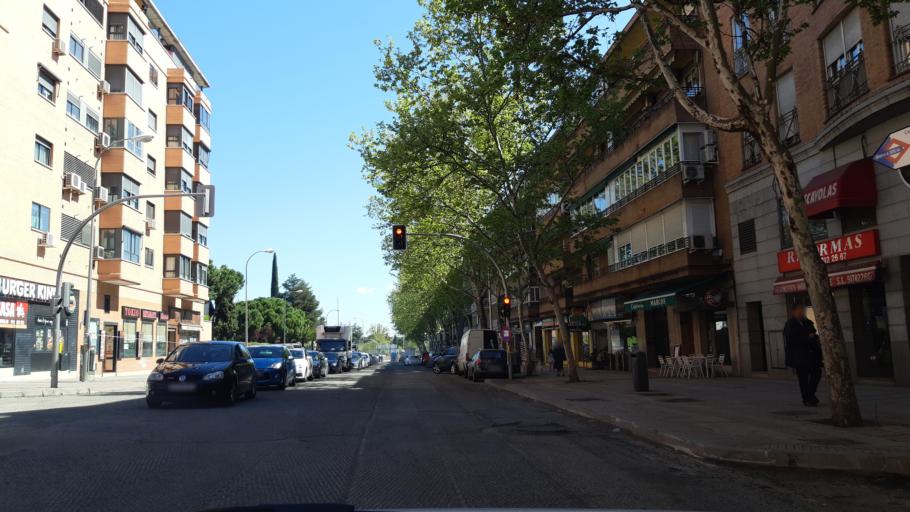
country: ES
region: Madrid
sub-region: Provincia de Madrid
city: San Blas
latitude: 40.4478
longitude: -3.6107
